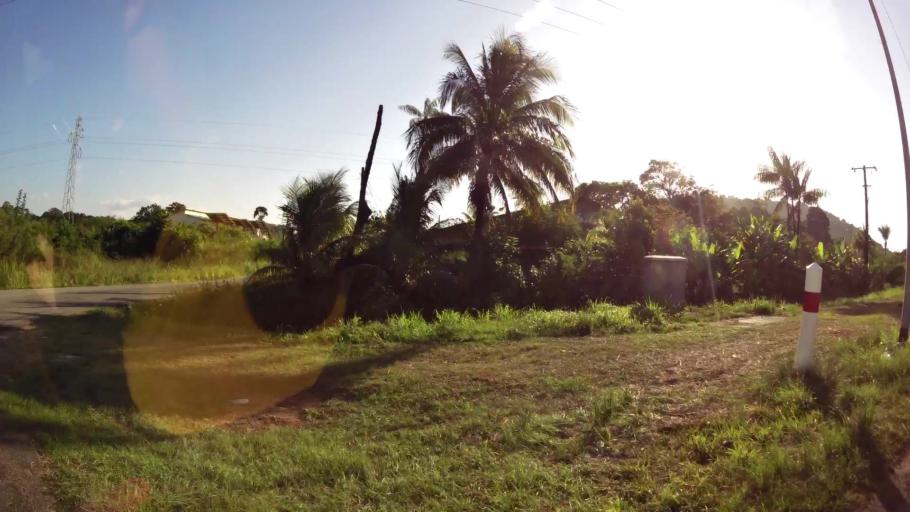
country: GF
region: Guyane
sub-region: Guyane
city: Remire-Montjoly
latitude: 4.8902
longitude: -52.2878
